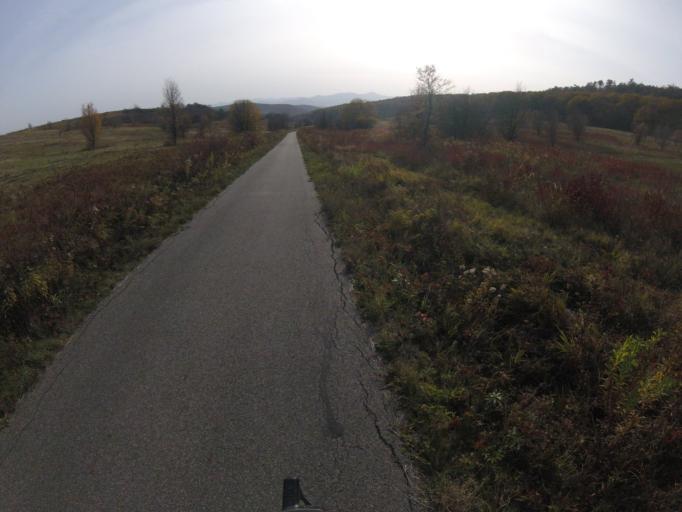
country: HU
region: Borsod-Abauj-Zemplen
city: Gonc
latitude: 48.5241
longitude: 21.4580
